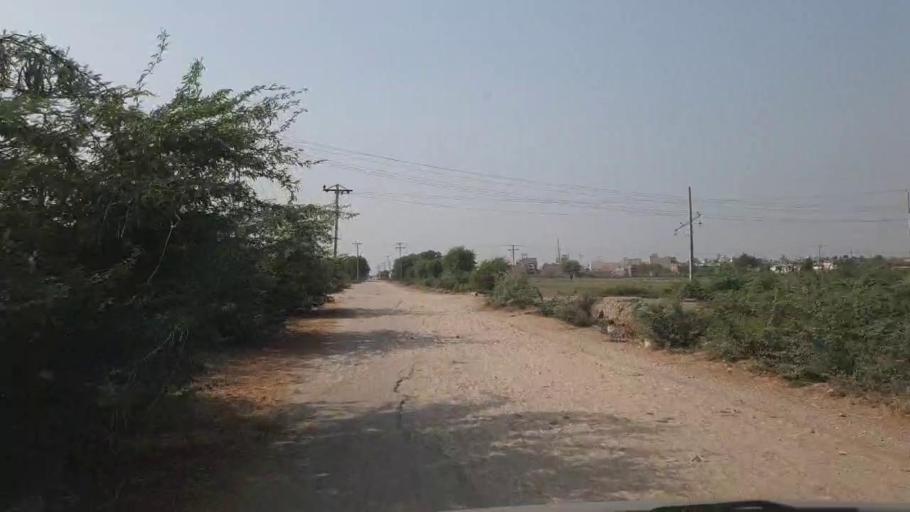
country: PK
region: Sindh
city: Matli
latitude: 25.0322
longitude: 68.6609
